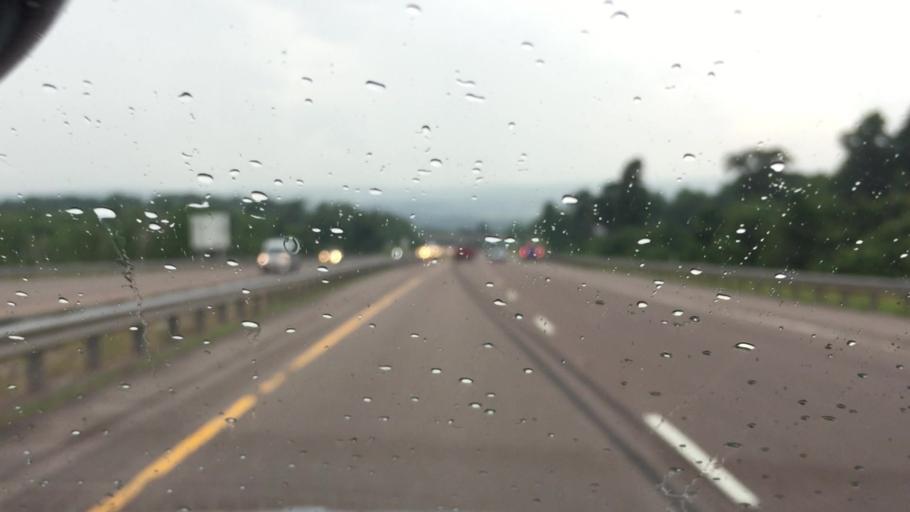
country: US
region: Pennsylvania
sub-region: Somerset County
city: Meyersdale
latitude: 39.6916
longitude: -79.1134
